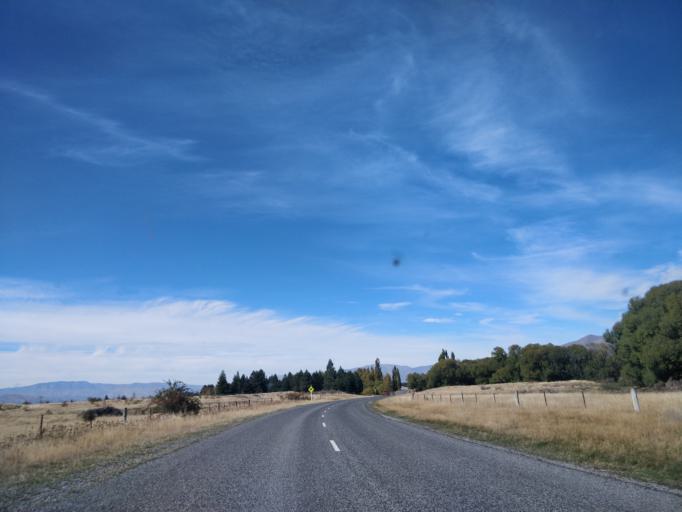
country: NZ
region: Otago
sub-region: Queenstown-Lakes District
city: Wanaka
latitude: -44.2222
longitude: 170.0562
